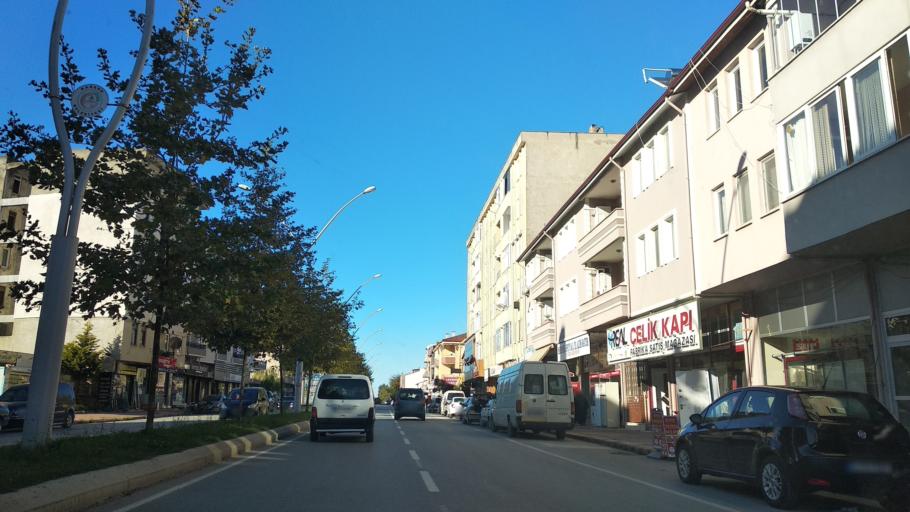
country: TR
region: Sakarya
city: Karasu
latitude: 41.1013
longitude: 30.6926
